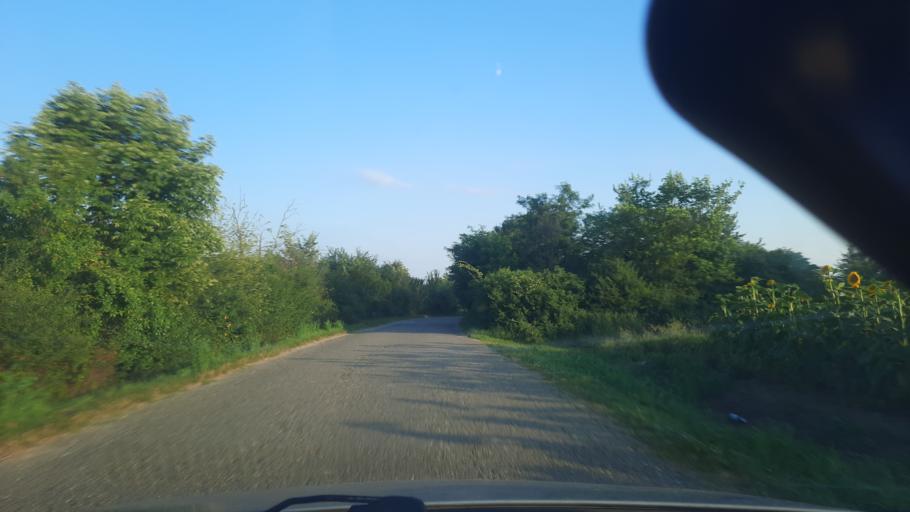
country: RS
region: Central Serbia
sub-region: Macvanski Okrug
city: Vladimirci
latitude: 44.6461
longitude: 19.8419
